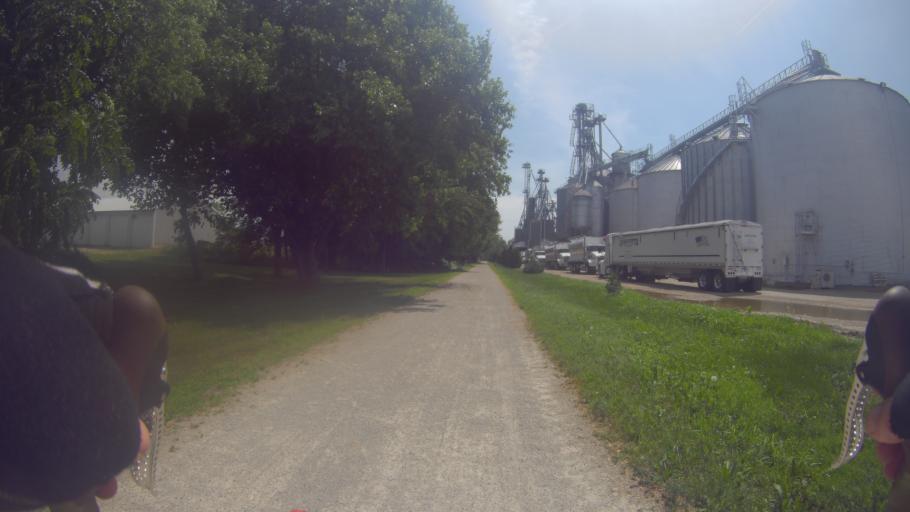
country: US
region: Wisconsin
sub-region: Jefferson County
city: Lake Mills
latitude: 43.0644
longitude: -88.9170
